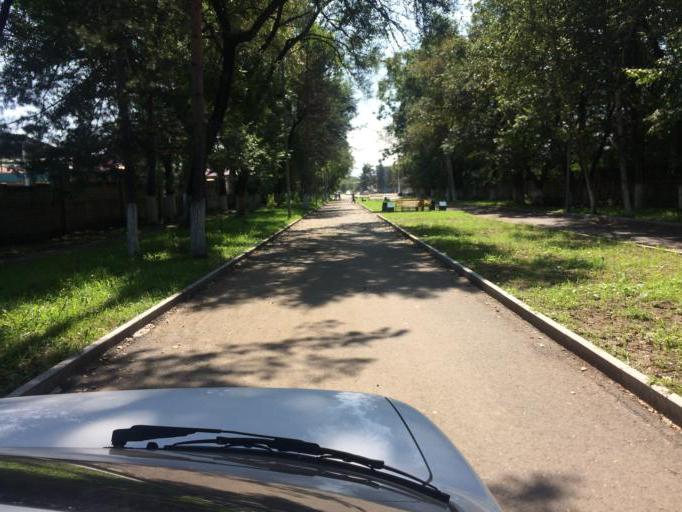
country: RU
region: Primorskiy
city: Dal'nerechensk
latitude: 45.9330
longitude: 133.7262
